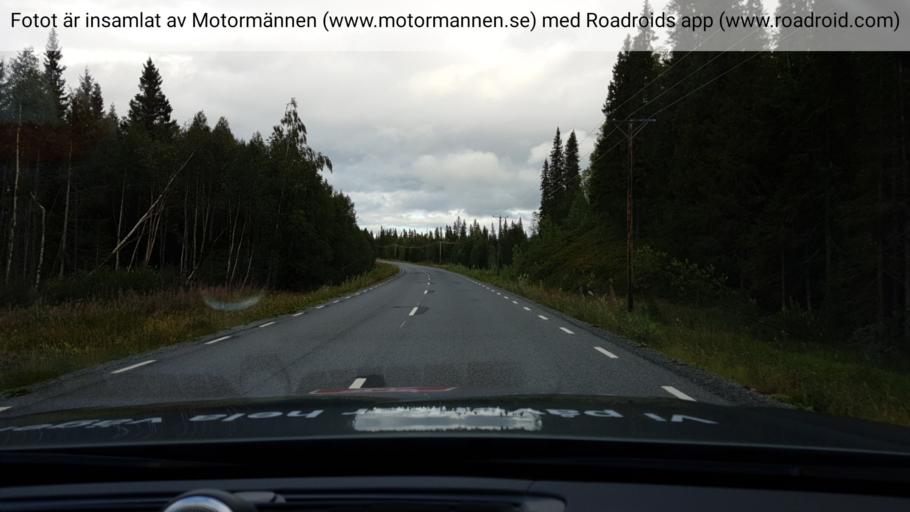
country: SE
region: Jaemtland
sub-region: Krokoms Kommun
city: Krokom
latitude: 63.6402
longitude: 14.4005
